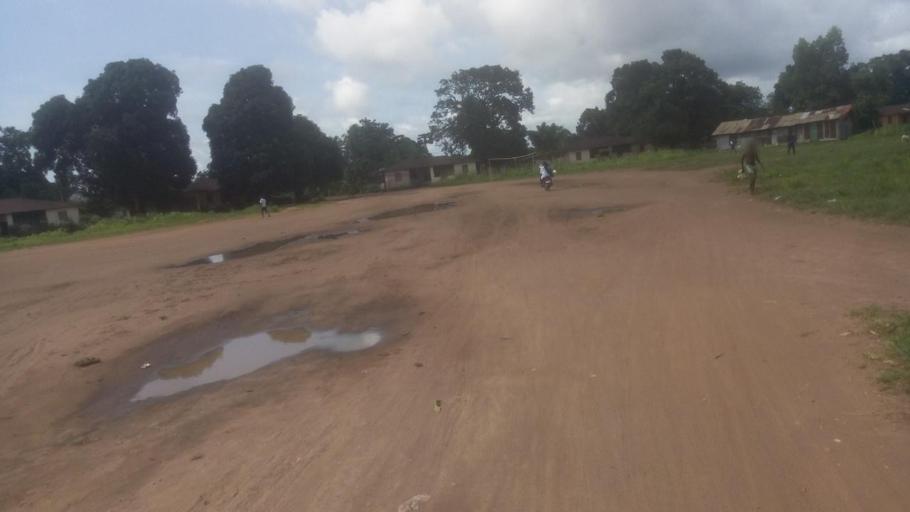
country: SL
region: Northern Province
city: Tintafor
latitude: 8.6262
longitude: -13.2152
